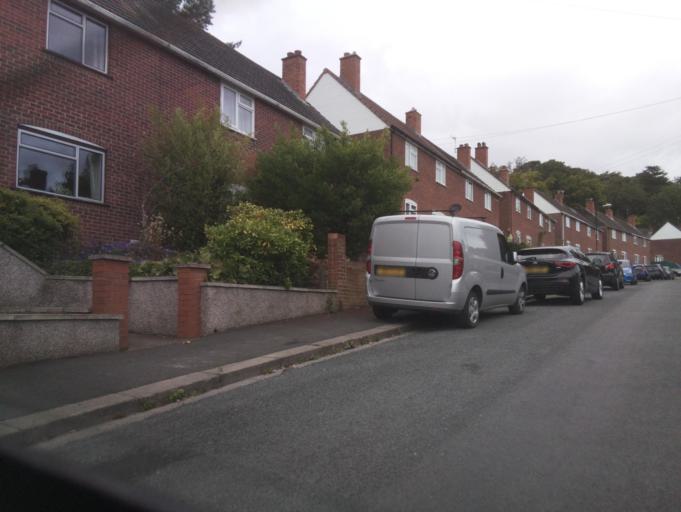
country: GB
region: England
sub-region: North Somerset
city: Easton-in-Gordano
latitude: 51.4935
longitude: -2.6509
